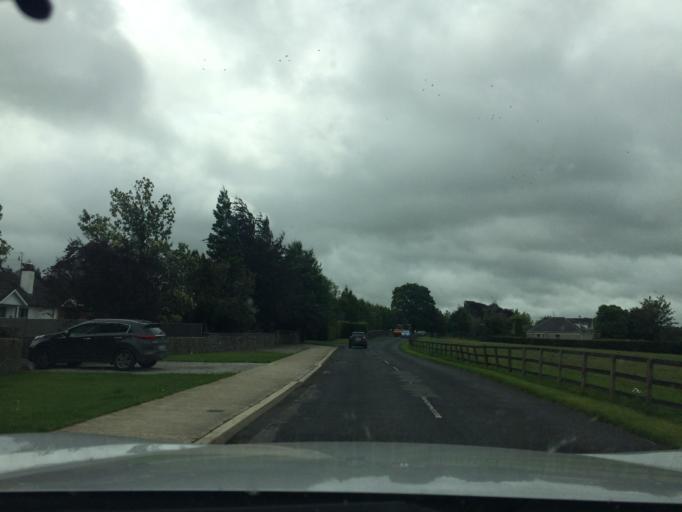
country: IE
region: Munster
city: Thurles
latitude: 52.6339
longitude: -7.8691
